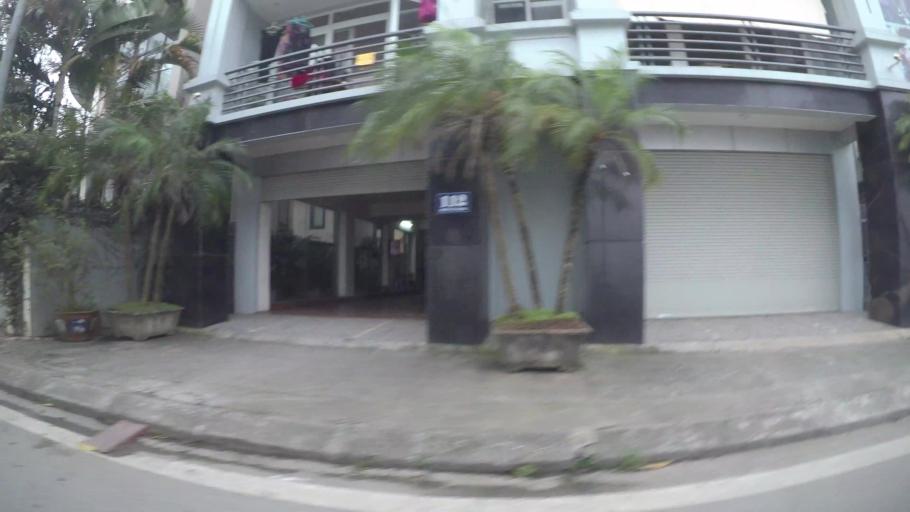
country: VN
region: Ha Noi
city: Tay Ho
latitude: 21.0582
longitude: 105.8289
